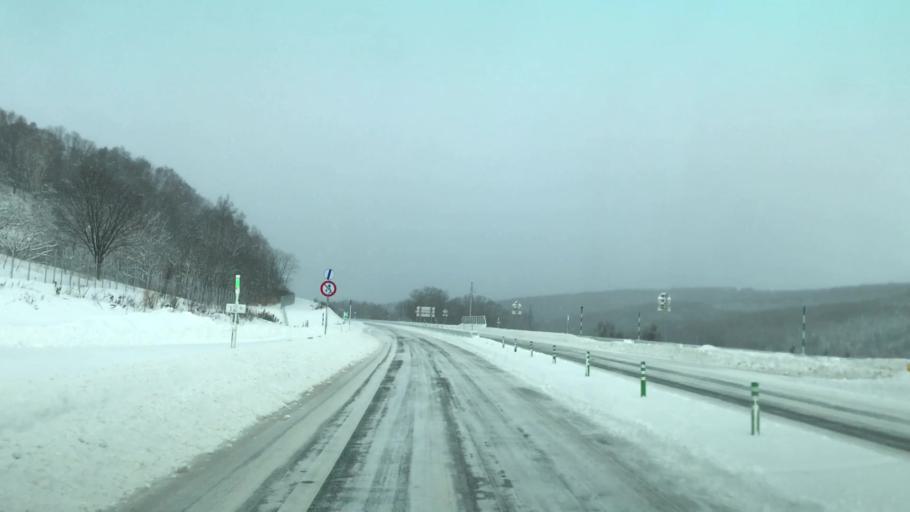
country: JP
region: Hokkaido
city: Otaru
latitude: 43.1967
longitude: 140.9506
